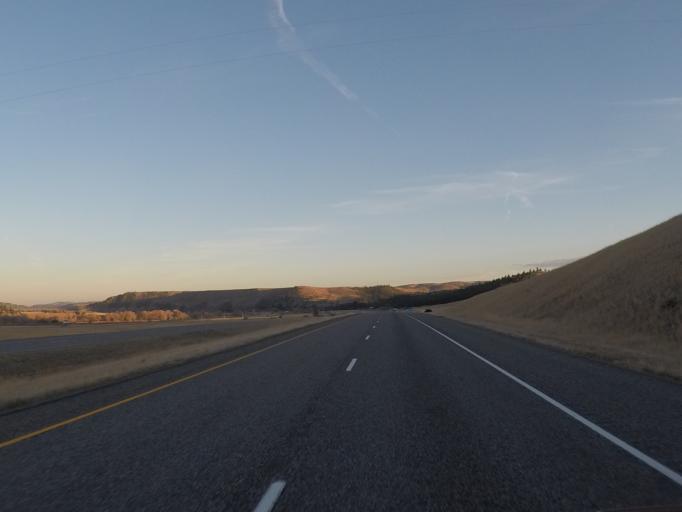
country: US
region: Montana
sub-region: Sweet Grass County
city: Big Timber
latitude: 45.7441
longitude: -109.7698
